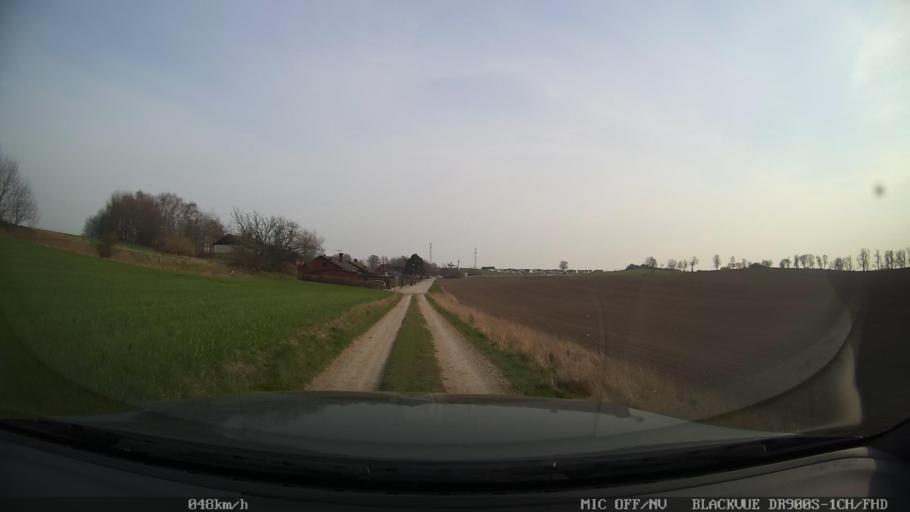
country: SE
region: Skane
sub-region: Ystads Kommun
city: Ystad
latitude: 55.4527
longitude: 13.7940
